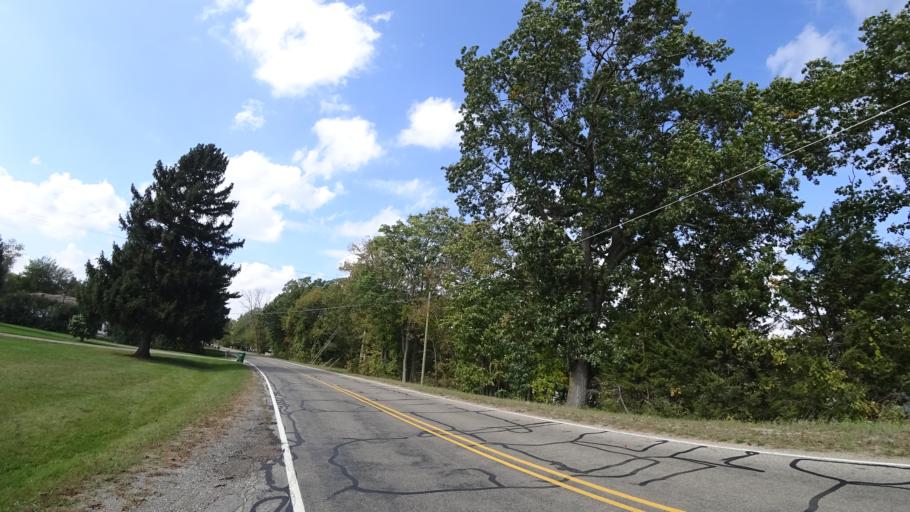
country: US
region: Michigan
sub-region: Saint Joseph County
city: Three Rivers
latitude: 41.9401
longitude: -85.6055
